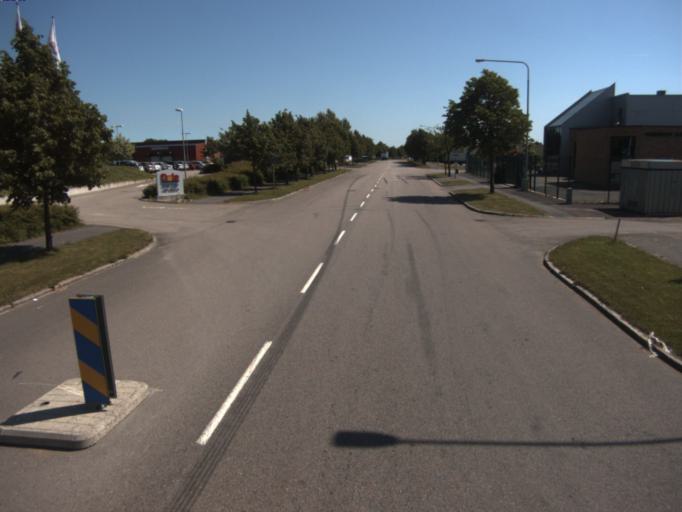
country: SE
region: Skane
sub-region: Helsingborg
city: Gantofta
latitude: 56.0071
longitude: 12.7693
